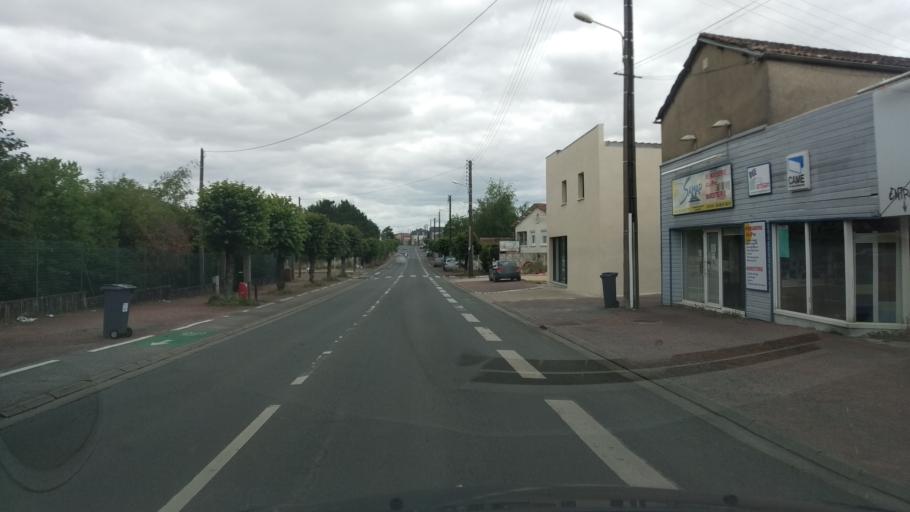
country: FR
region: Poitou-Charentes
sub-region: Departement de la Vienne
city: Poitiers
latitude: 46.5943
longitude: 0.3281
